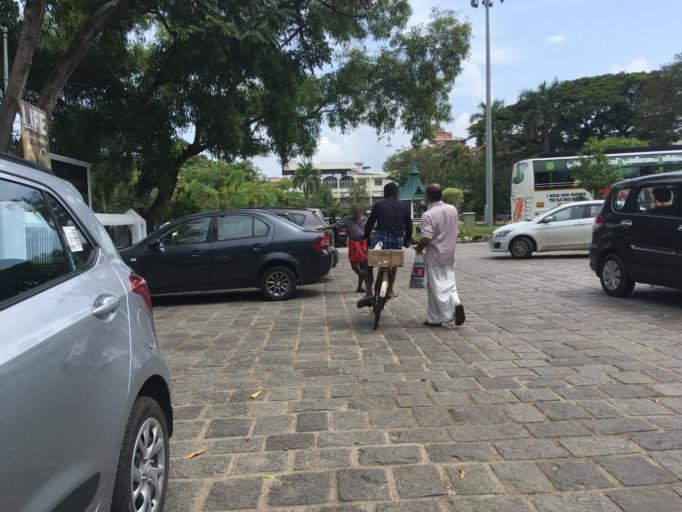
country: IN
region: Kerala
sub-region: Ernakulam
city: Cochin
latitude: 9.9685
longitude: 76.2836
